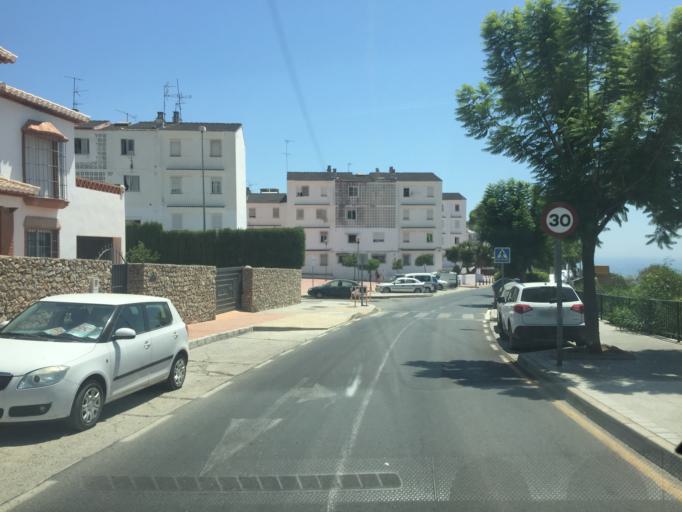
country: ES
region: Andalusia
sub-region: Provincia de Malaga
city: Nerja
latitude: 36.7642
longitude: -3.8714
